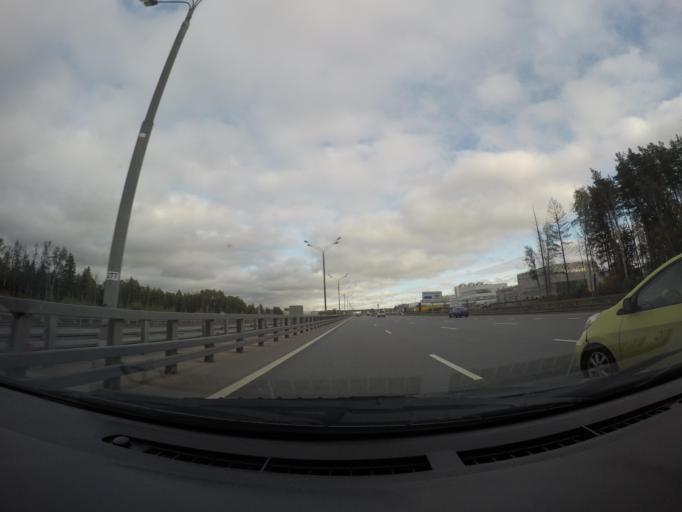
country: RU
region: Moskovskaya
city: Krasnoznamensk
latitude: 55.6045
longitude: 37.0149
